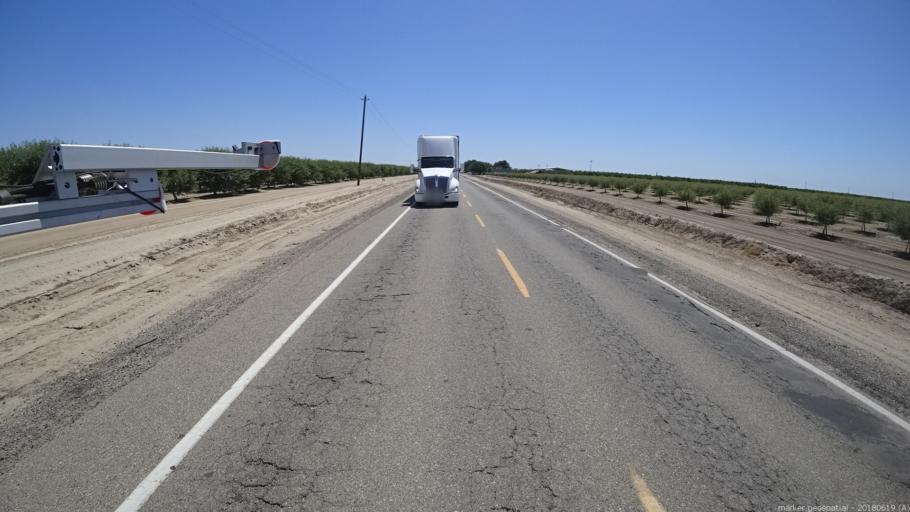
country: US
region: California
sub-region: Fresno County
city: Mendota
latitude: 36.8511
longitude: -120.2772
